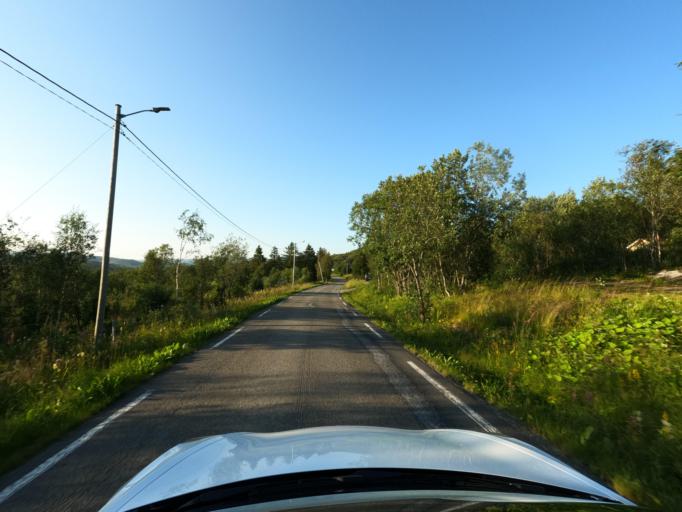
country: NO
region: Nordland
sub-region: Ballangen
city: Ballangen
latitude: 68.4960
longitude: 16.7352
